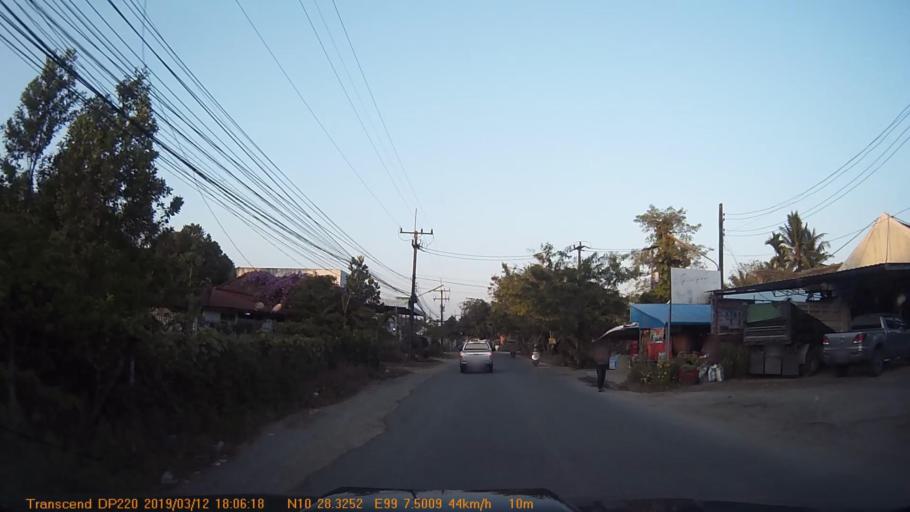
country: TH
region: Chumphon
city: Chumphon
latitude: 10.4722
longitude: 99.1251
